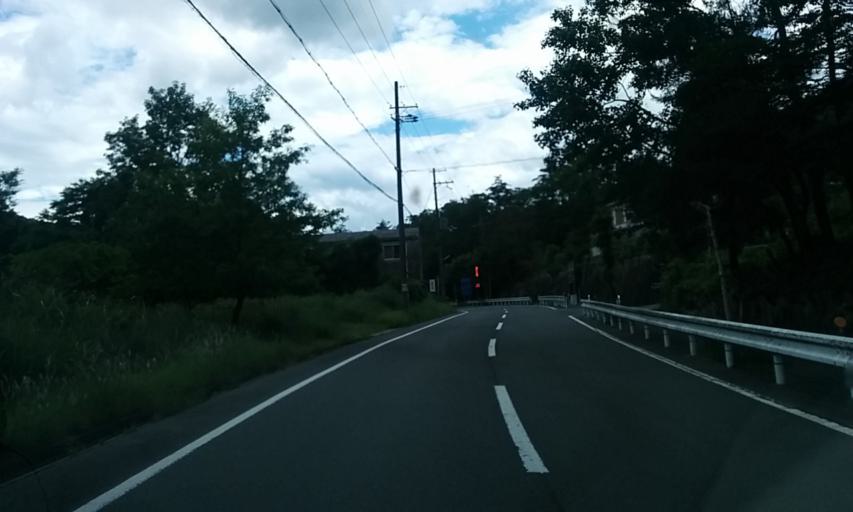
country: JP
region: Kyoto
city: Kameoka
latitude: 35.0081
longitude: 135.4318
